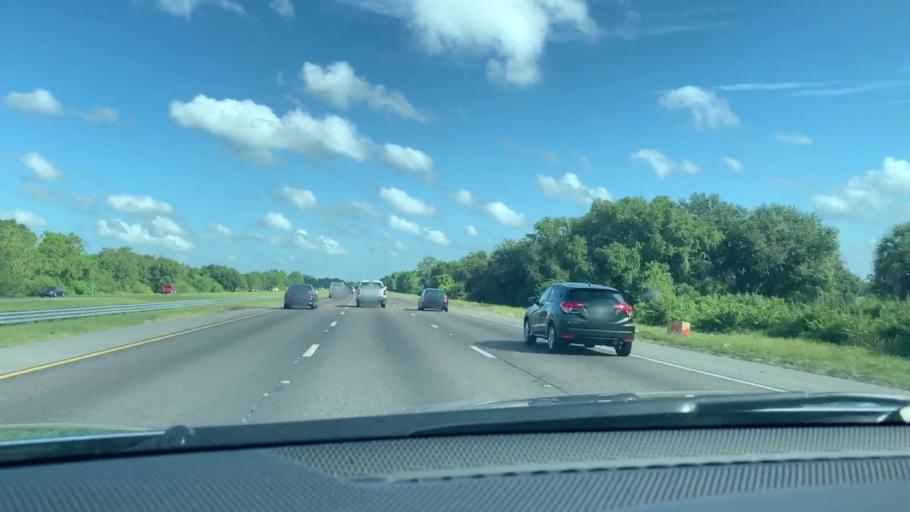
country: US
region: Florida
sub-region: Hillsborough County
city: Gibsonton
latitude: 27.8128
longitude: -82.3517
